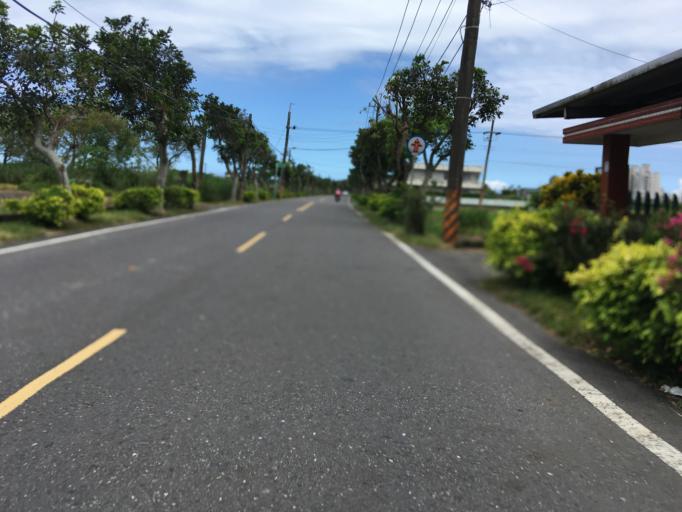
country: TW
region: Taiwan
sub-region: Yilan
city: Yilan
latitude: 24.6843
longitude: 121.8048
